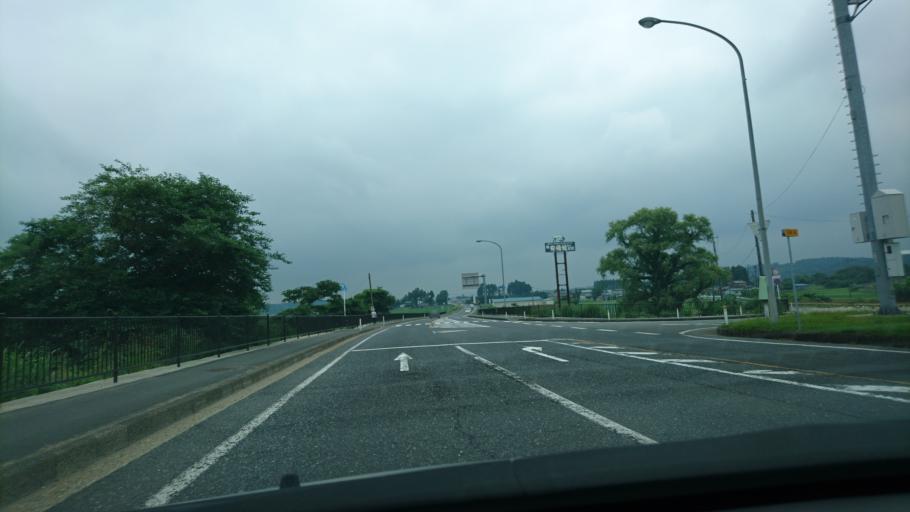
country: JP
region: Miyagi
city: Furukawa
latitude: 38.6767
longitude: 140.8613
